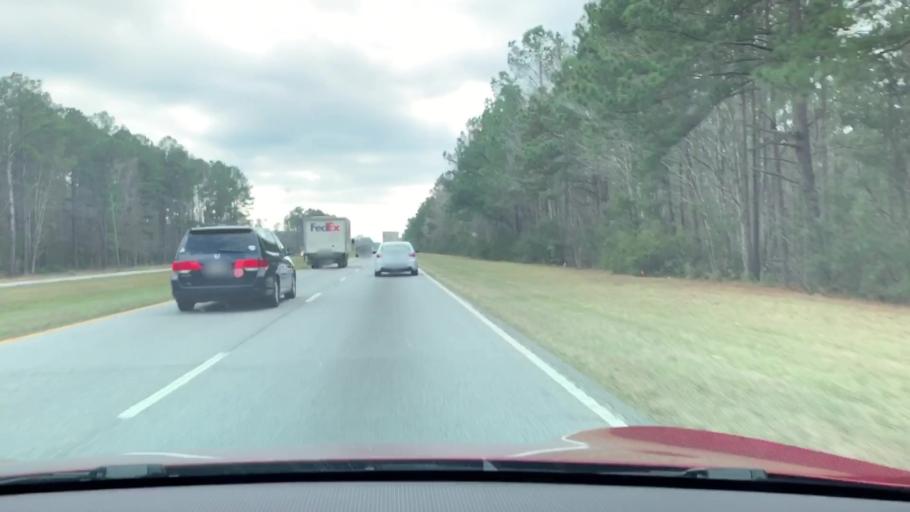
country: US
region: South Carolina
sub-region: Jasper County
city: Hardeeville
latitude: 32.2514
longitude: -81.0777
